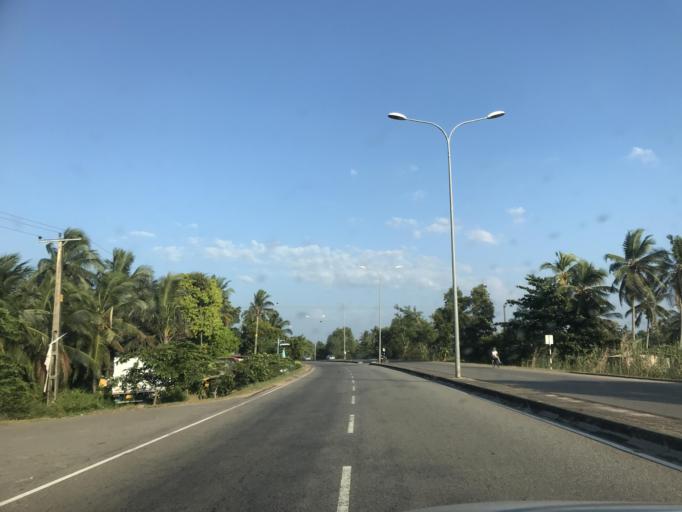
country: LK
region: Western
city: Ja Ela
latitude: 7.0814
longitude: 79.8823
